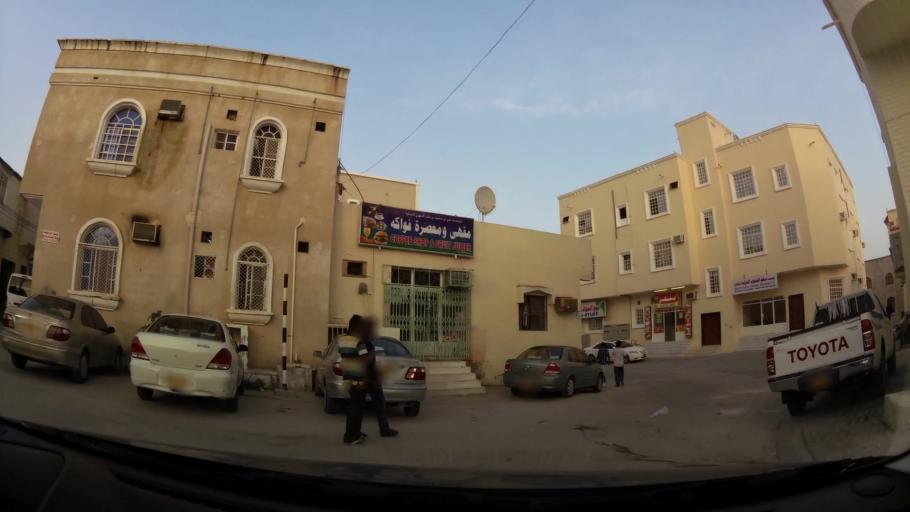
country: OM
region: Zufar
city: Salalah
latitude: 17.0198
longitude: 54.1240
